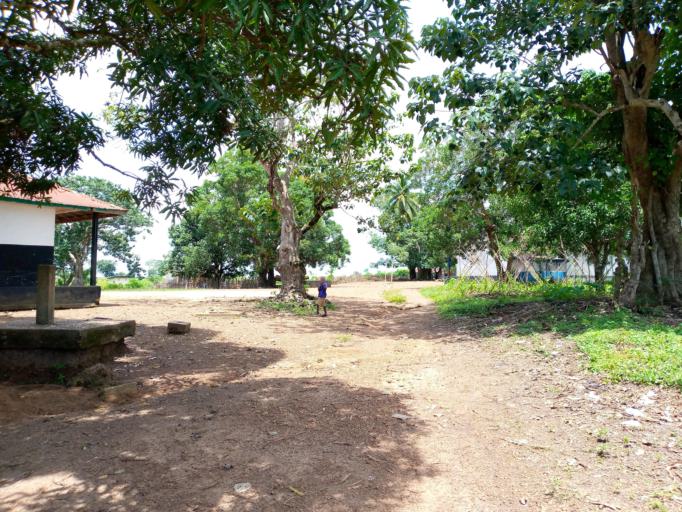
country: SL
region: Northern Province
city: Magburaka
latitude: 8.7140
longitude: -11.9539
